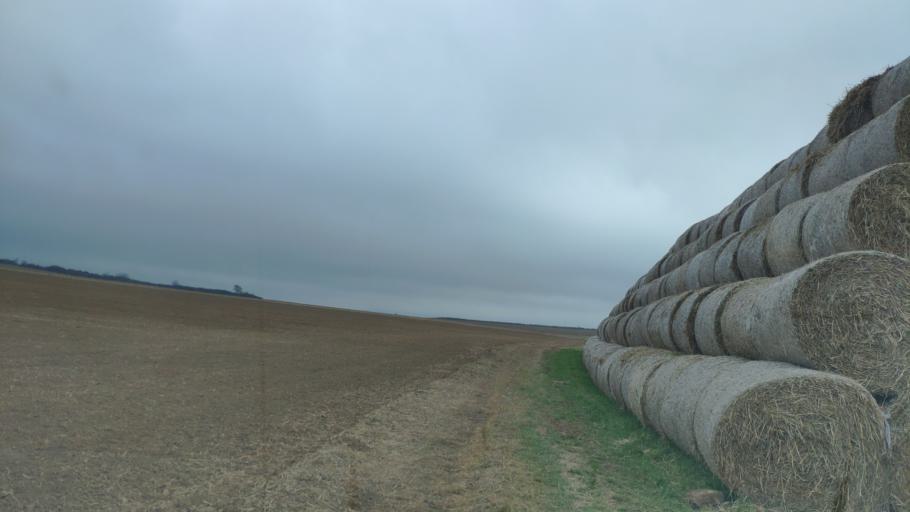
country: SK
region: Presovsky
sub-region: Okres Presov
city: Presov
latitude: 49.0168
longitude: 21.2049
